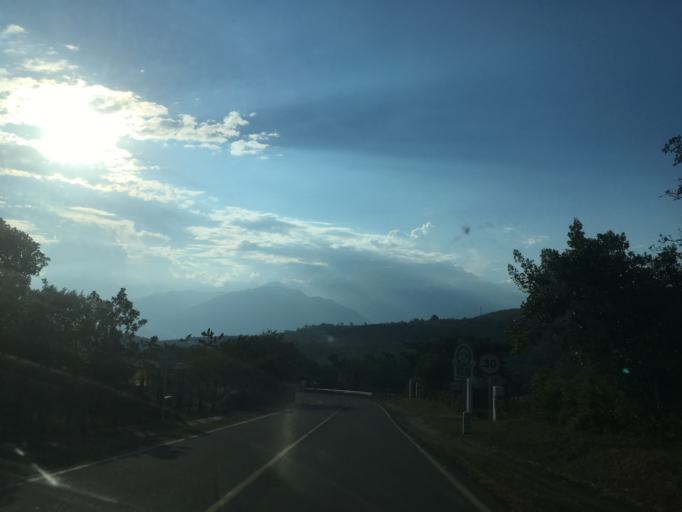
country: CO
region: Santander
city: Barichara
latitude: 6.6408
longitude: -73.1950
